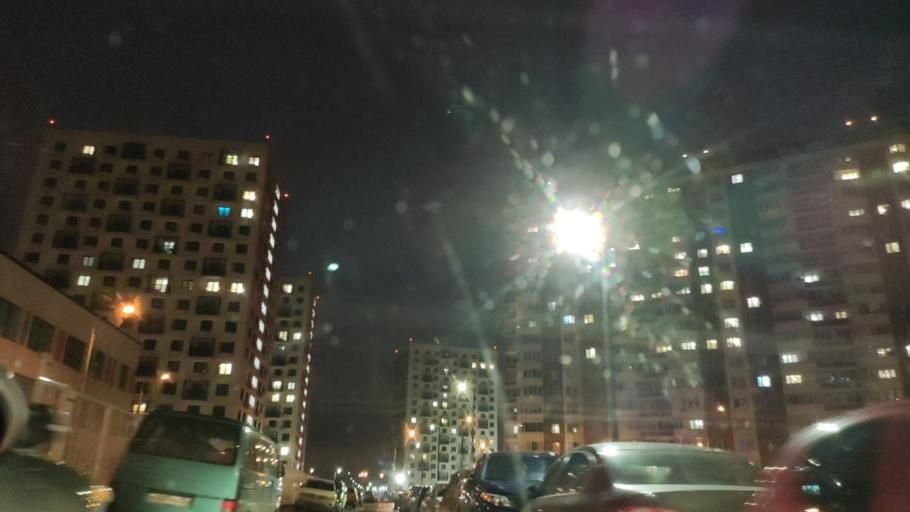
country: RU
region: Moscow
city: Annino
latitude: 55.5292
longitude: 37.6169
